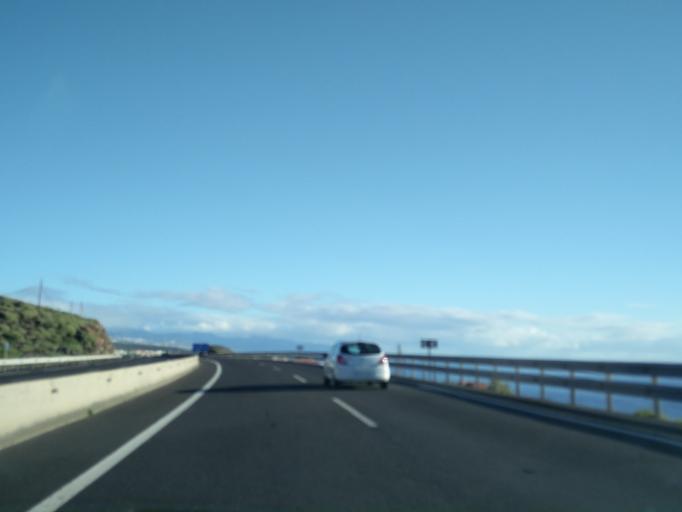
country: ES
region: Canary Islands
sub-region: Provincia de Santa Cruz de Tenerife
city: Fasnia
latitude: 28.2635
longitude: -16.3901
